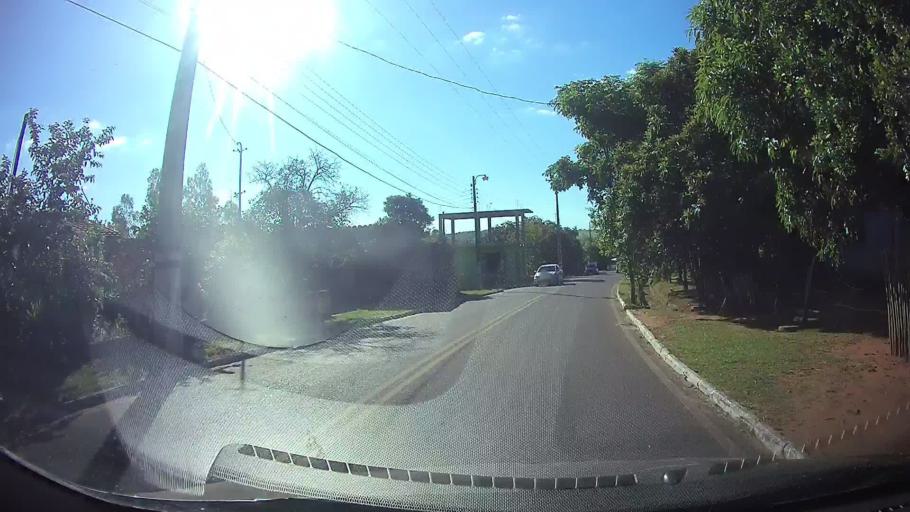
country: PY
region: Cordillera
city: Atyra
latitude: -25.2842
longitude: -57.1721
